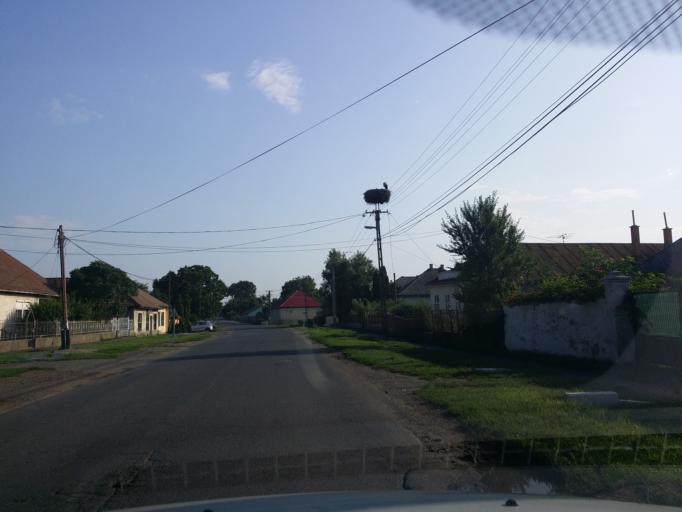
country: HU
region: Borsod-Abauj-Zemplen
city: Gonc
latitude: 48.4160
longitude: 21.2312
